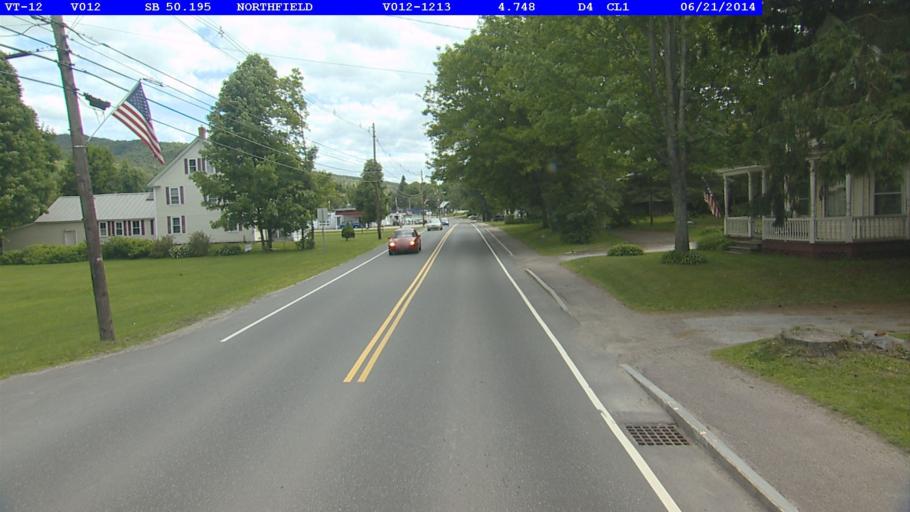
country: US
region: Vermont
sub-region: Washington County
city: Northfield
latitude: 44.1568
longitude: -72.6570
